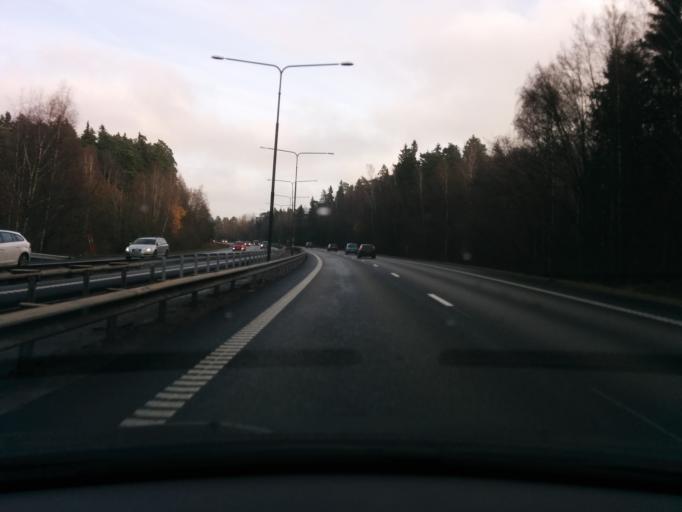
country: SE
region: Vaestmanland
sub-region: Vasteras
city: Vasteras
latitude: 59.6166
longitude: 16.5063
